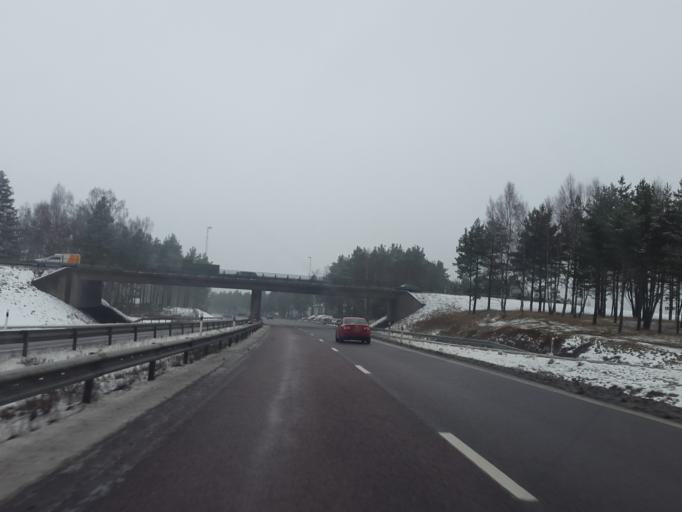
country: SE
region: Joenkoeping
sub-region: Jonkopings Kommun
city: Jonkoping
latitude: 57.7634
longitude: 14.1017
